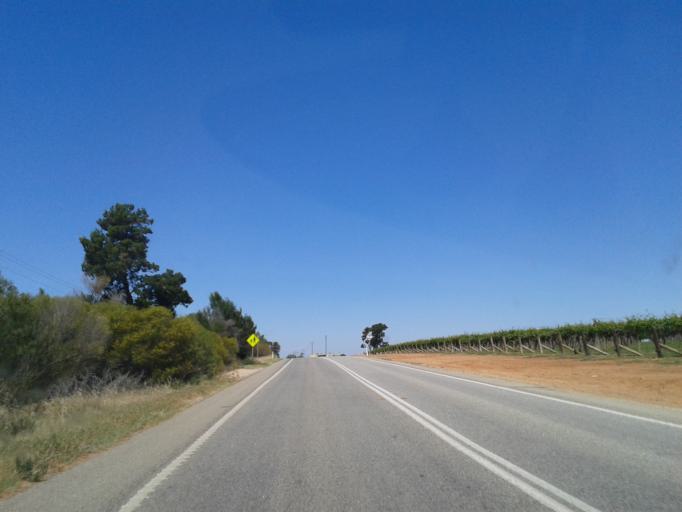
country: AU
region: Victoria
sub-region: Mildura Shire
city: Ouyen
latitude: -34.6061
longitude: 142.7919
